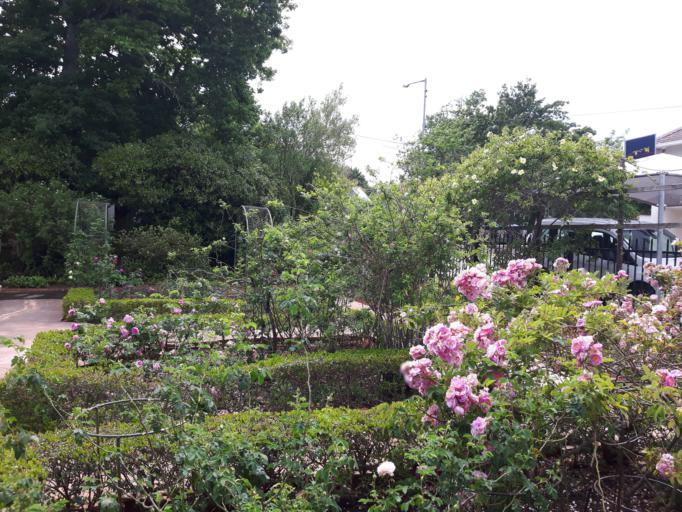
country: ZA
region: Western Cape
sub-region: Overberg District Municipality
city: Swellendam
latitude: -34.0183
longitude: 20.4515
